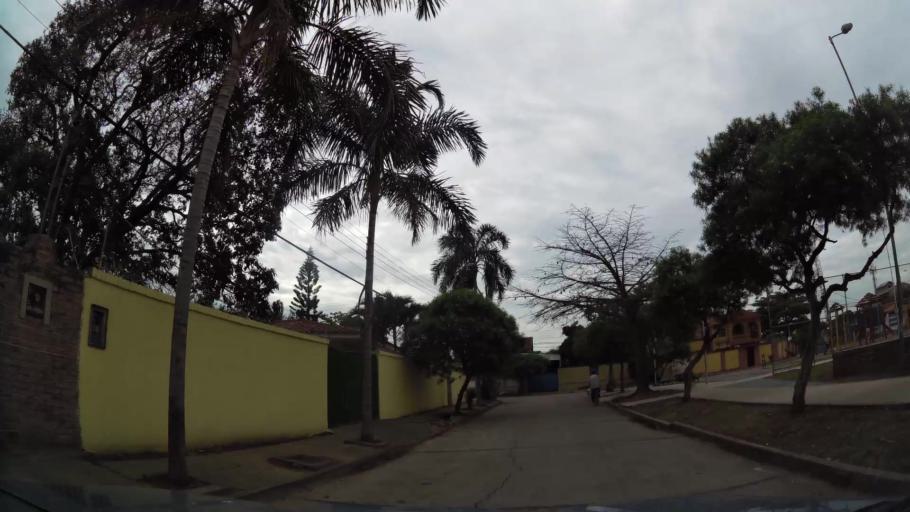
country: BO
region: Santa Cruz
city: Santa Cruz de la Sierra
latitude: -17.7673
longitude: -63.1611
